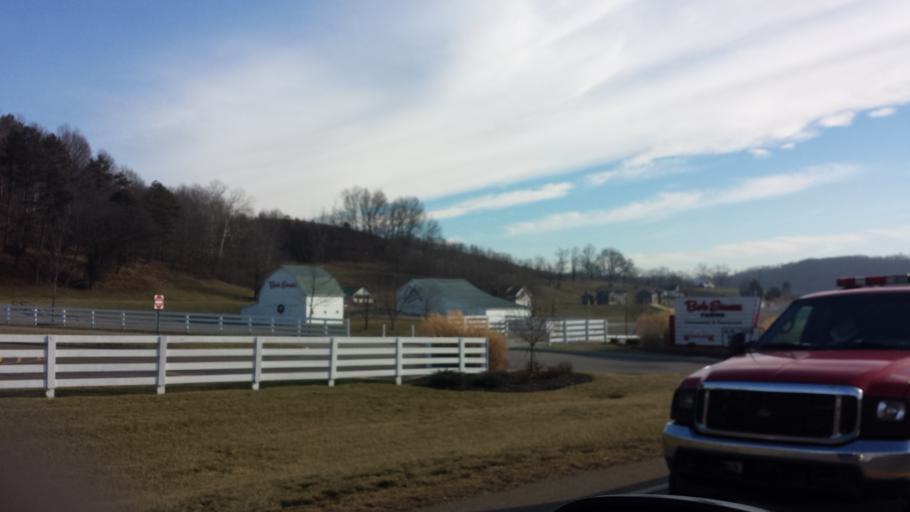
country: US
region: Ohio
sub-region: Gallia County
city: Gallipolis
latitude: 38.8818
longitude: -82.3684
